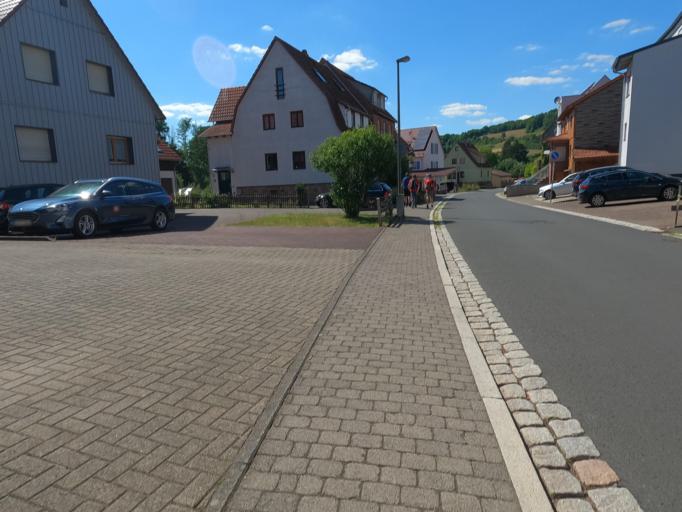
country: DE
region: Hesse
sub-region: Regierungsbezirk Darmstadt
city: Schluchtern
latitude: 50.3577
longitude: 9.5586
